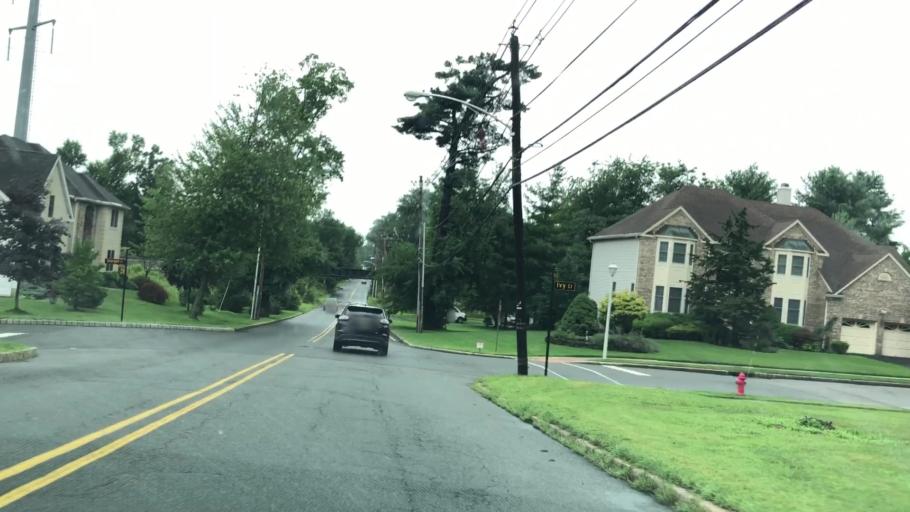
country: US
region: New Jersey
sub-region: Morris County
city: East Hanover
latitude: 40.8198
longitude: -74.3482
